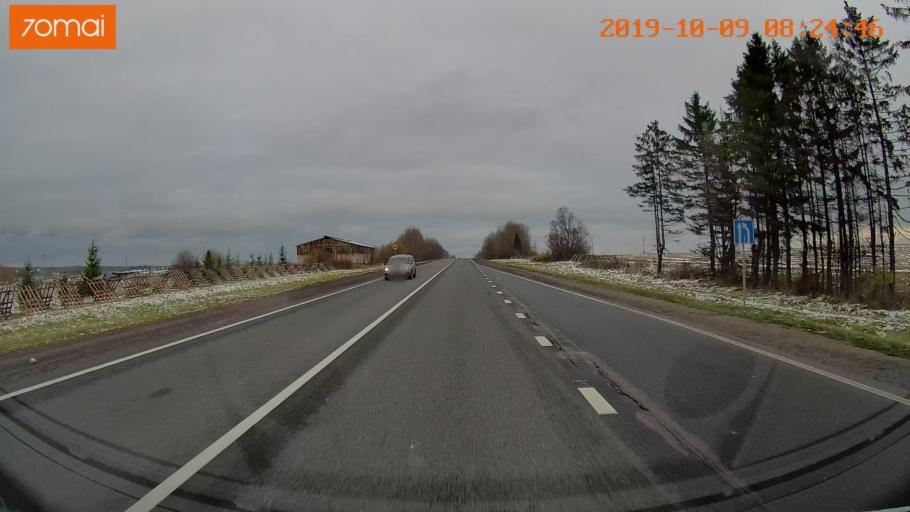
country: RU
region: Vologda
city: Gryazovets
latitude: 58.7711
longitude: 40.2764
